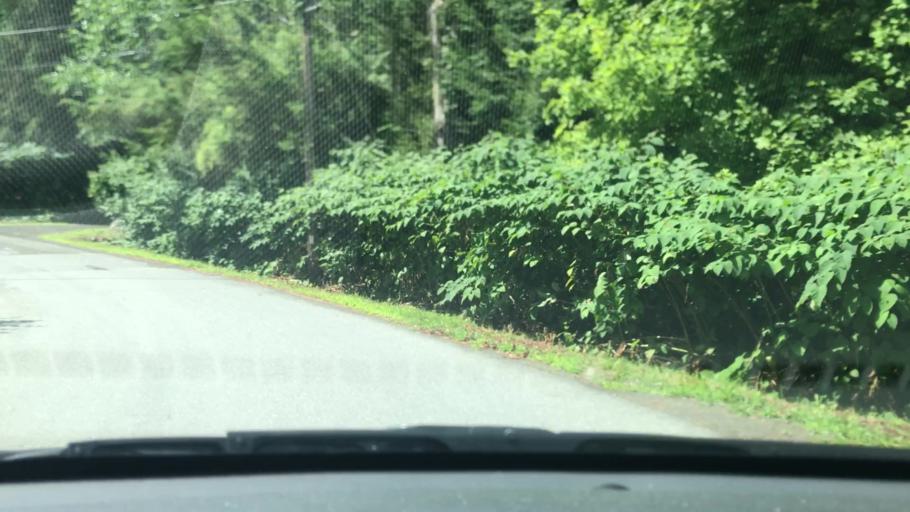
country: US
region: New York
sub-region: Ulster County
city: Shokan
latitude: 41.9667
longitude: -74.2867
